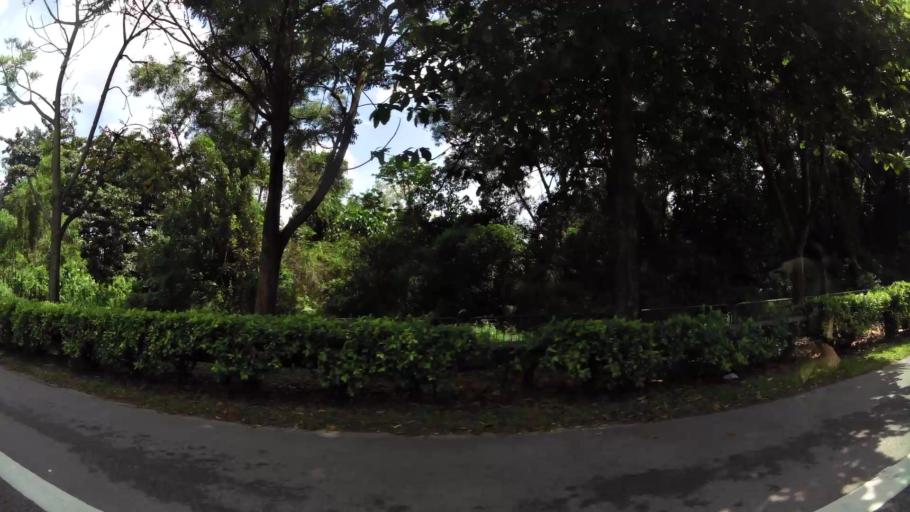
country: MY
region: Johor
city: Johor Bahru
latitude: 1.4007
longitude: 103.7738
